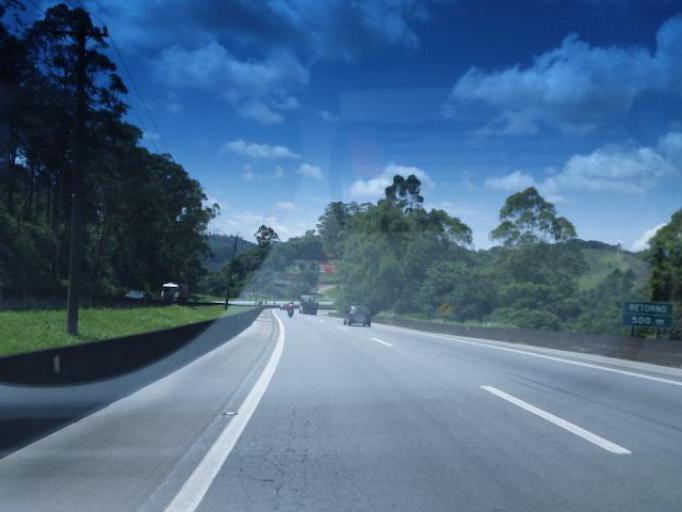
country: BR
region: Sao Paulo
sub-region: Sao Lourenco Da Serra
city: Sao Lourenco da Serra
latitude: -23.7952
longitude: -46.9153
